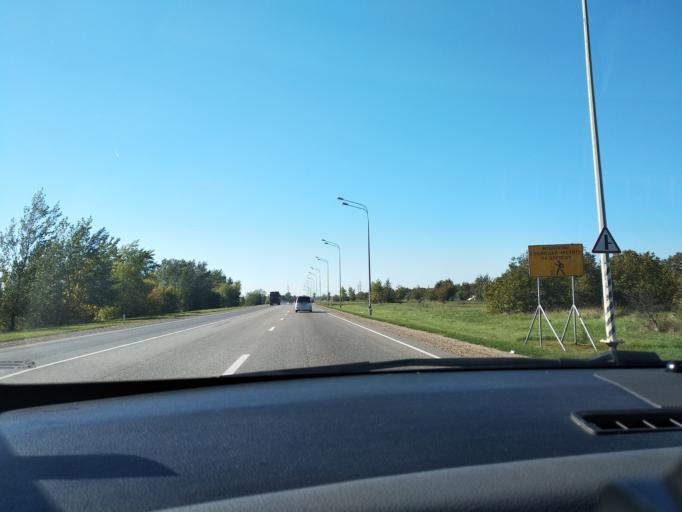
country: RU
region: Krasnodarskiy
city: Agronom
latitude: 45.1656
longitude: 39.0868
